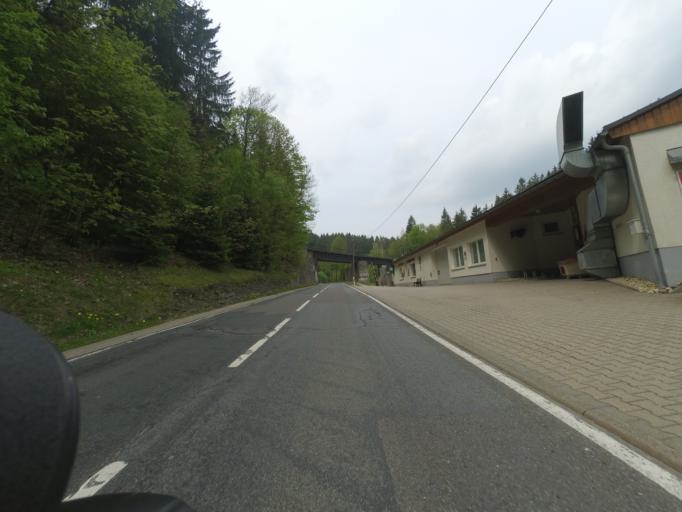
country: DE
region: Saxony
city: Pobershau
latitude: 50.6526
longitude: 13.2016
